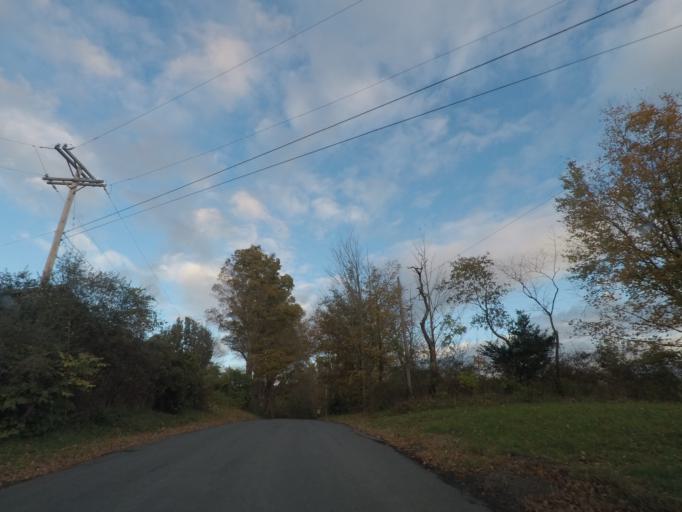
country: US
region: New York
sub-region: Rensselaer County
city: Nassau
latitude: 42.5448
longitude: -73.5875
